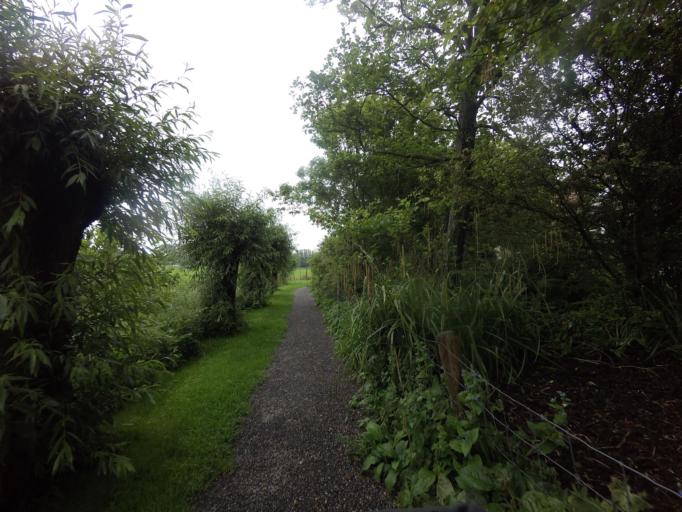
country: NL
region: North Holland
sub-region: Gemeente Schagen
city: Schagen
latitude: 52.7778
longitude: 4.7941
